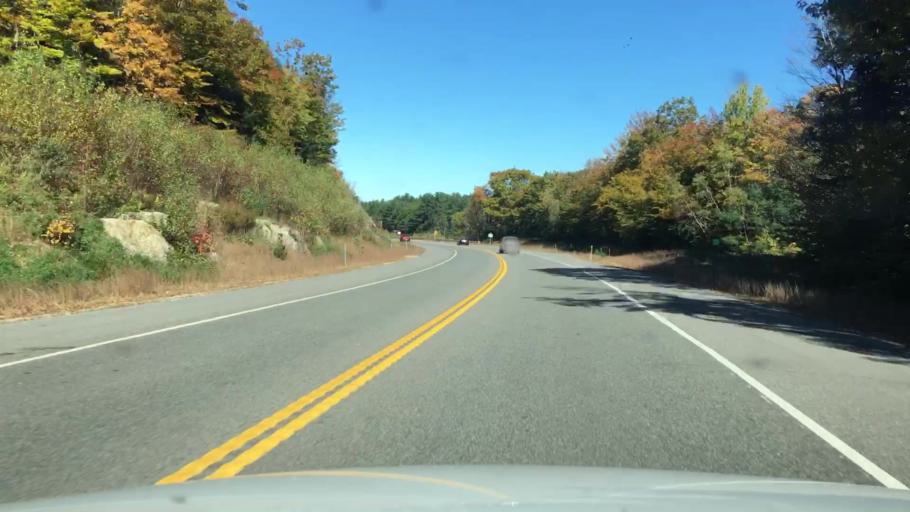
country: US
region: New Hampshire
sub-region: Carroll County
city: Sanbornville
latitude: 43.5258
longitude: -71.0260
